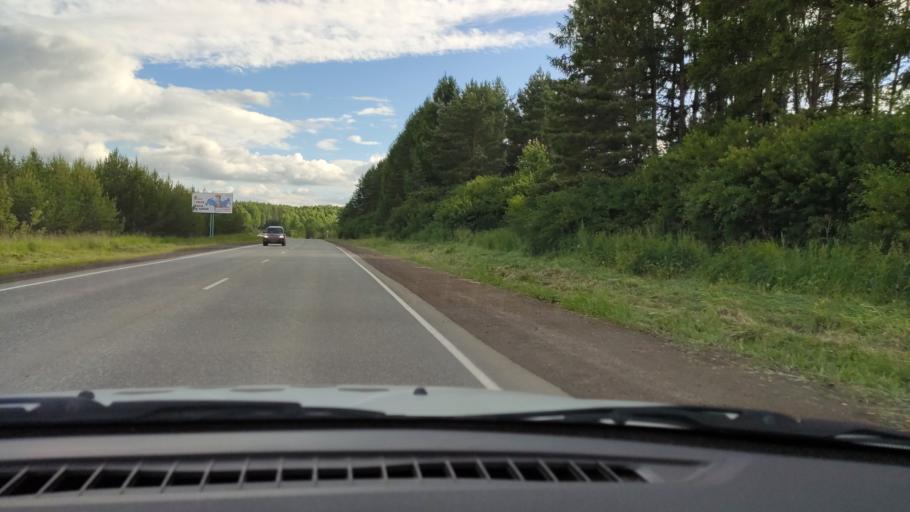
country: RU
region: Perm
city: Kungur
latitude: 57.4181
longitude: 56.9173
